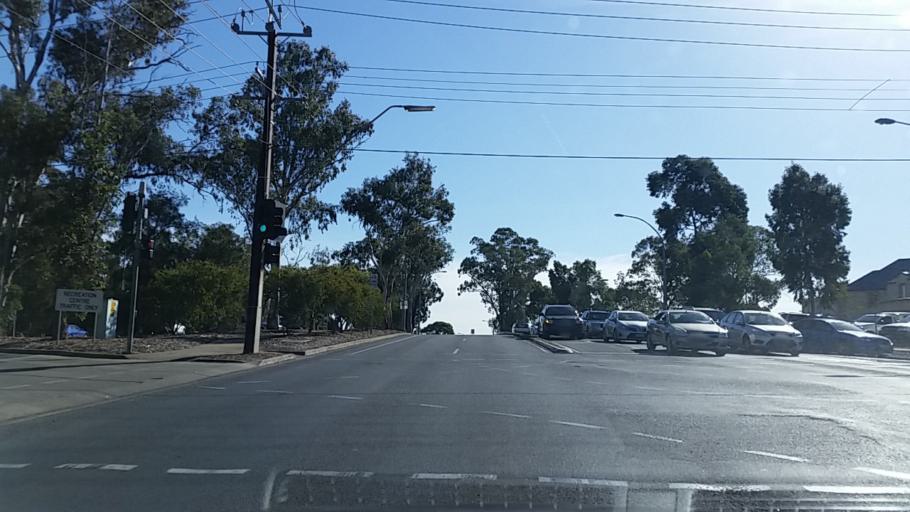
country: AU
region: South Australia
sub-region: Campbelltown
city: Athelstone
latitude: -34.8526
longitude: 138.7026
